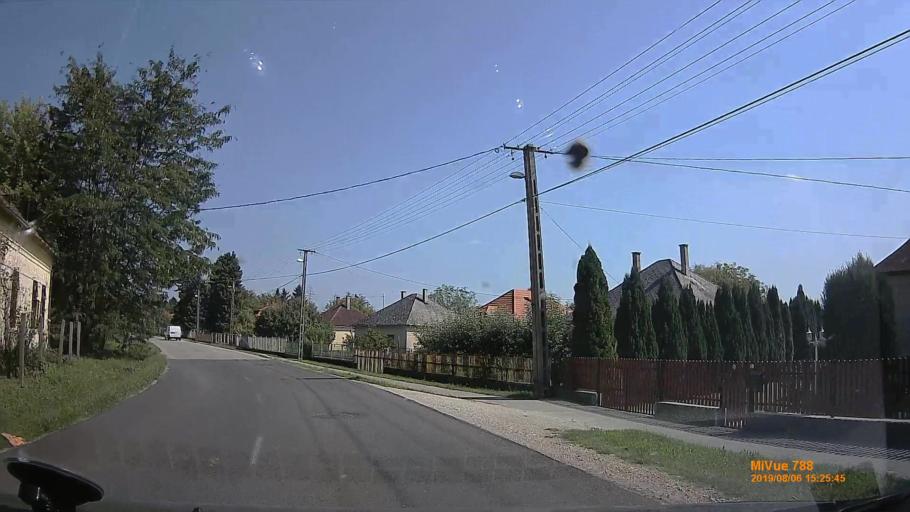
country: HR
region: Koprivnicko-Krizevacka
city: Drnje
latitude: 46.2521
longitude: 16.9481
